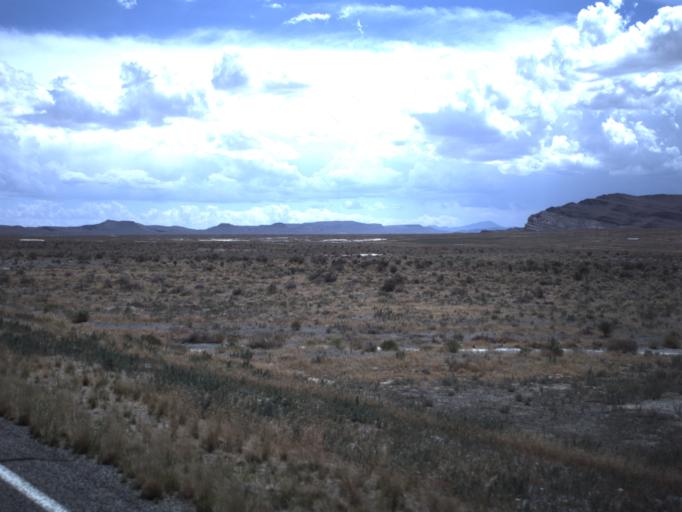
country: US
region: Utah
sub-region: Beaver County
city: Milford
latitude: 39.0383
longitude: -113.3965
